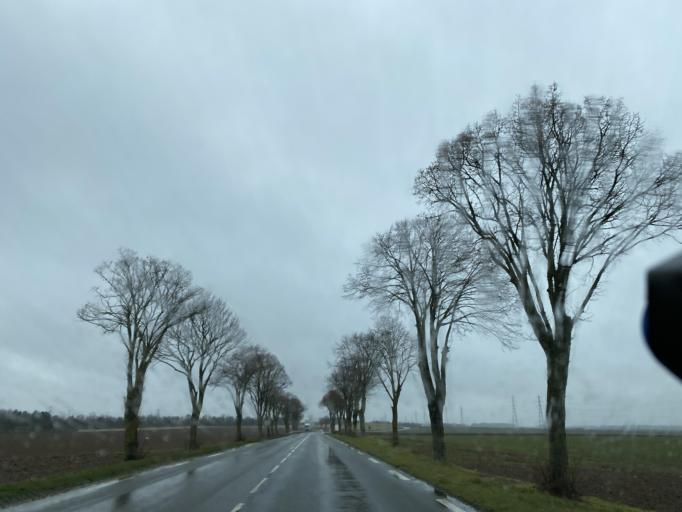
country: FR
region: Centre
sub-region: Departement d'Eure-et-Loir
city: Baigneaux
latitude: 48.1394
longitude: 1.8498
